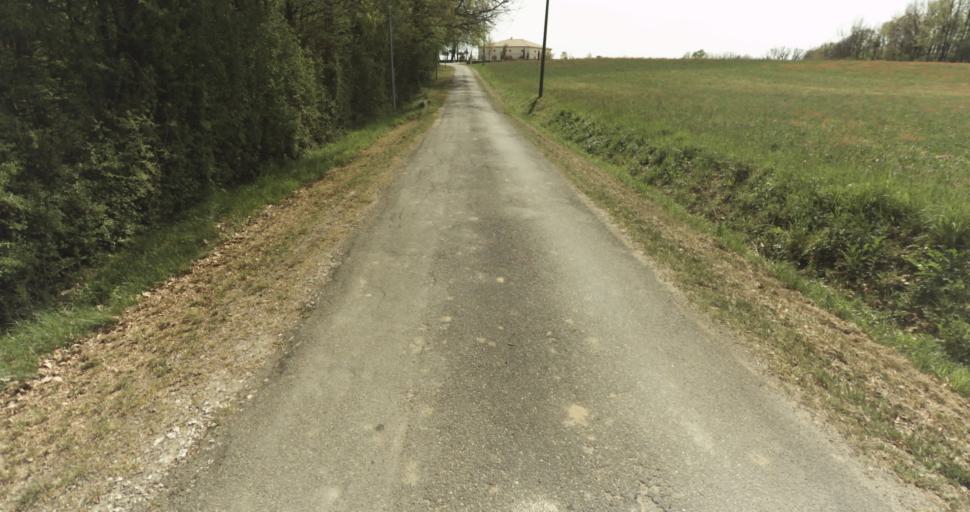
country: FR
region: Midi-Pyrenees
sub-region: Departement du Tarn-et-Garonne
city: Moissac
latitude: 44.1645
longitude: 1.0734
